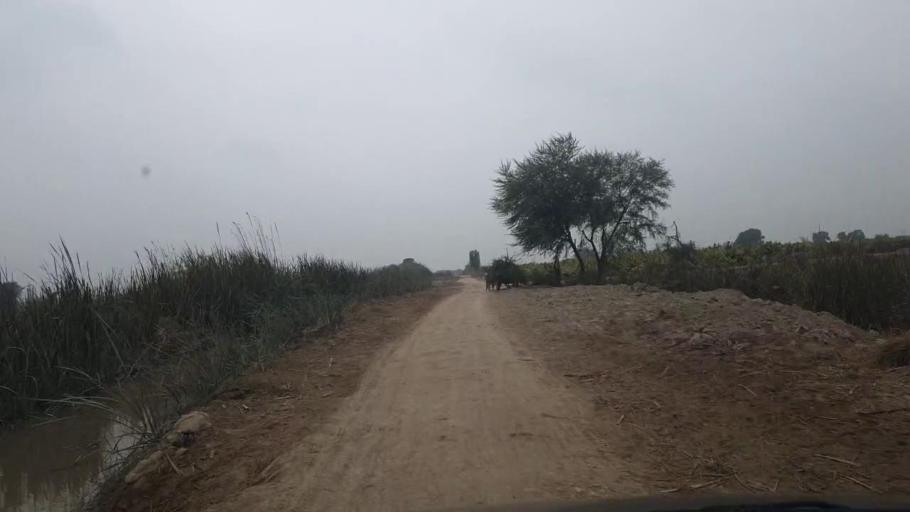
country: PK
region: Sindh
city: Tando Adam
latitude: 25.8459
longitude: 68.6794
